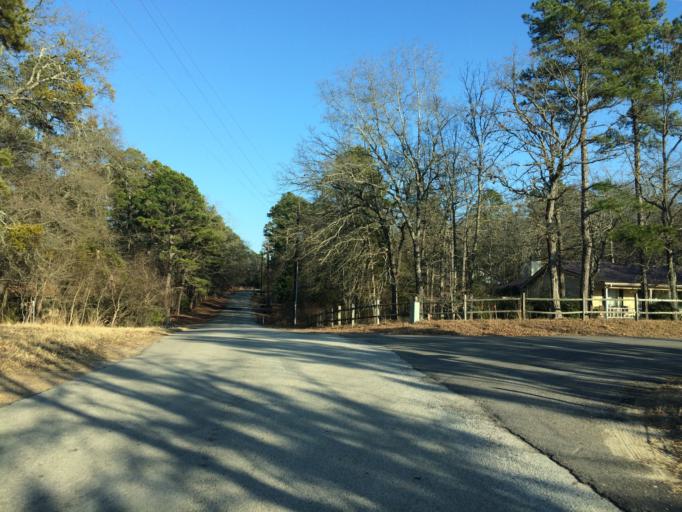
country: US
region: Texas
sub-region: Wood County
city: Hawkins
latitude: 32.7204
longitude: -95.1726
